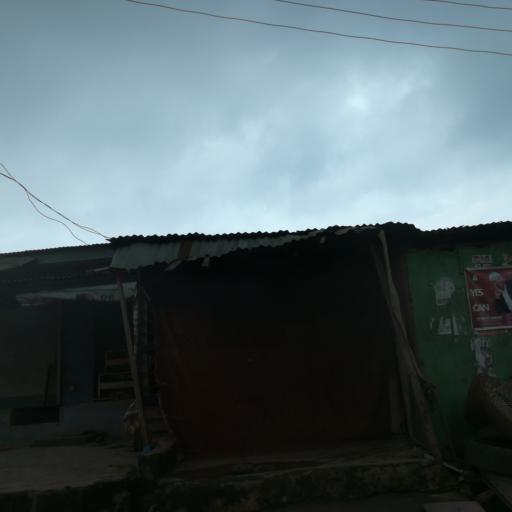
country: NG
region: Lagos
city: Agege
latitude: 6.5940
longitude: 3.3026
